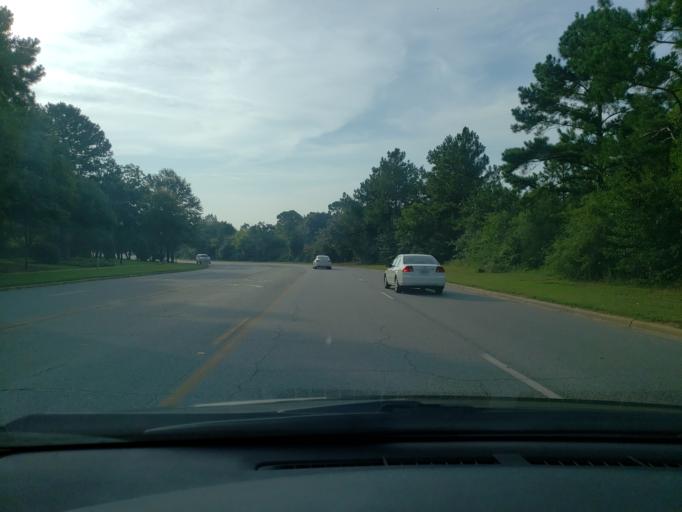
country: US
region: Georgia
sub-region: Dougherty County
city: Albany
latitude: 31.6089
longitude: -84.2148
